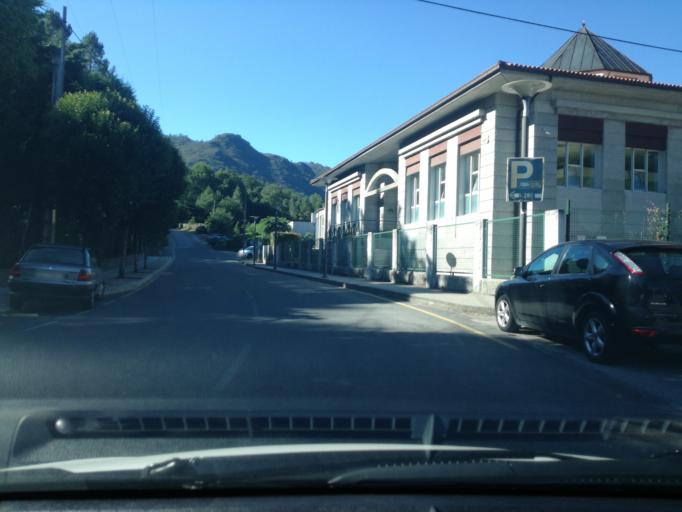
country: ES
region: Galicia
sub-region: Provincia de Ourense
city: Lobios
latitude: 41.8621
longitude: -8.1064
